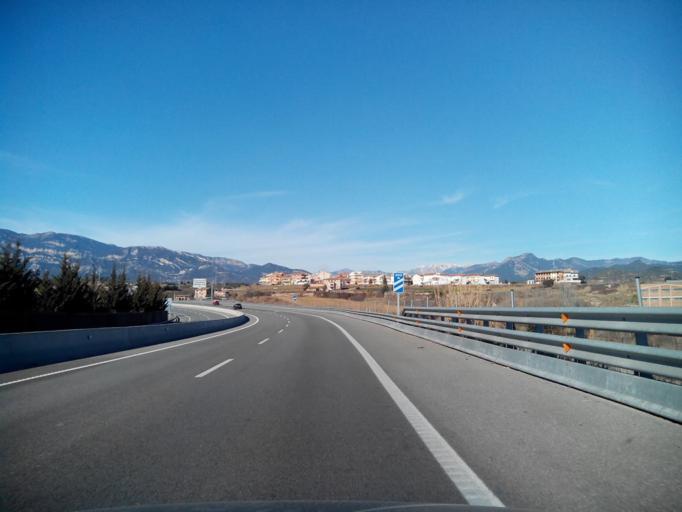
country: ES
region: Catalonia
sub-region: Provincia de Barcelona
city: Gironella
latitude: 42.0263
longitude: 1.8769
